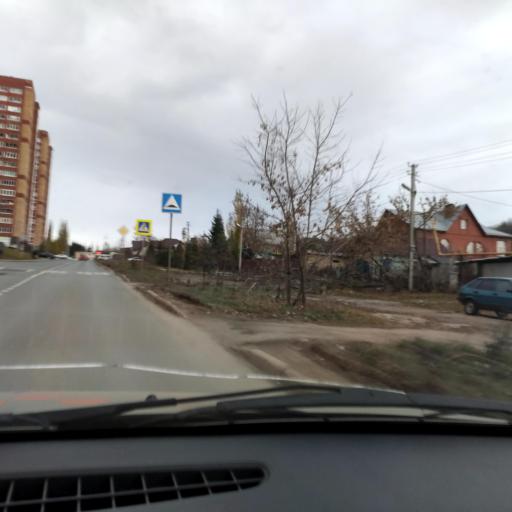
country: RU
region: Bashkortostan
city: Ufa
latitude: 54.6883
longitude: 55.9978
